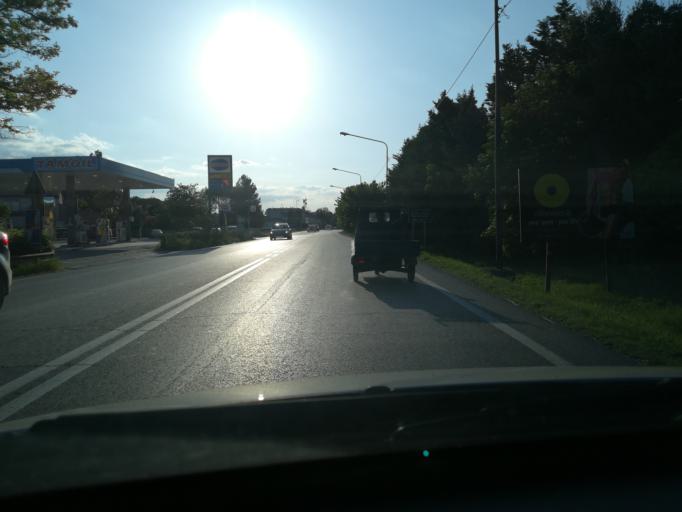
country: IT
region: Emilia-Romagna
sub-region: Provincia di Rimini
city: Riccione
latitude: 44.0013
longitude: 12.6388
